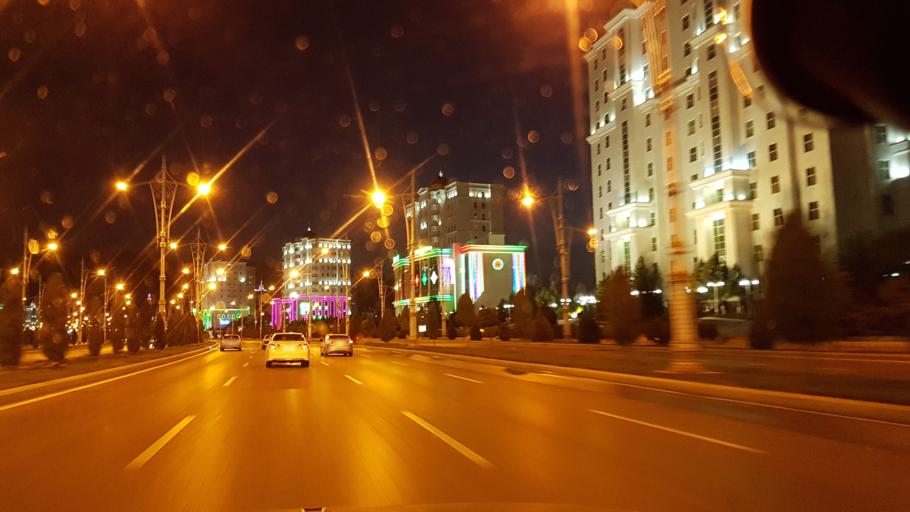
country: TM
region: Ahal
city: Ashgabat
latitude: 37.9174
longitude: 58.3481
